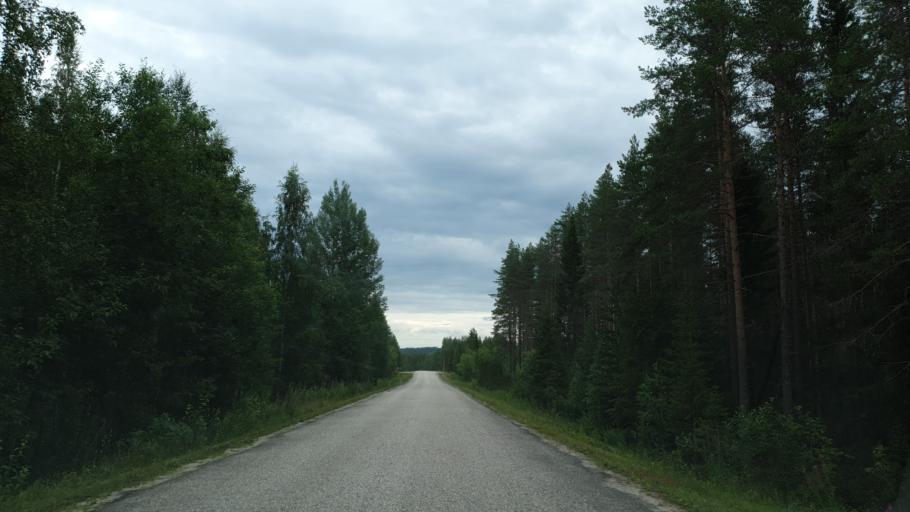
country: FI
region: Kainuu
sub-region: Kehys-Kainuu
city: Kuhmo
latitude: 64.3452
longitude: 29.2754
